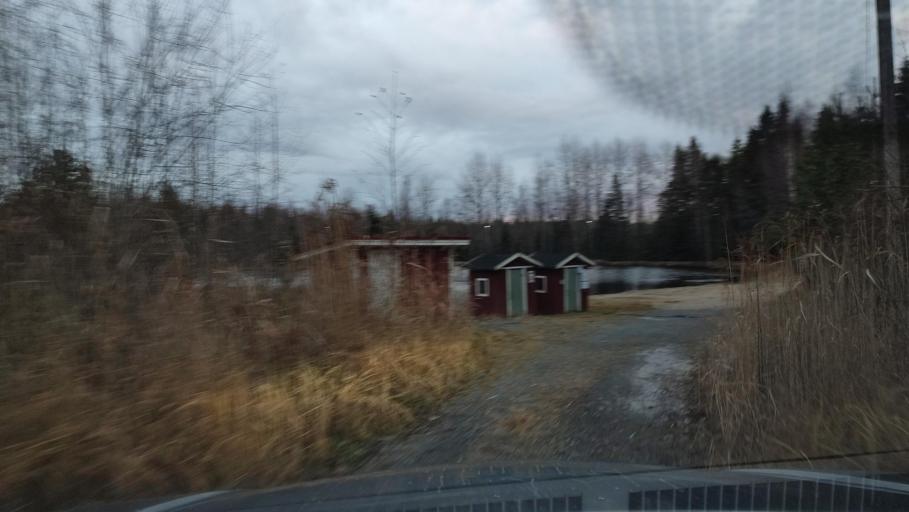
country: FI
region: Southern Ostrobothnia
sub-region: Suupohja
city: Karijoki
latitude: 62.2813
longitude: 21.6300
